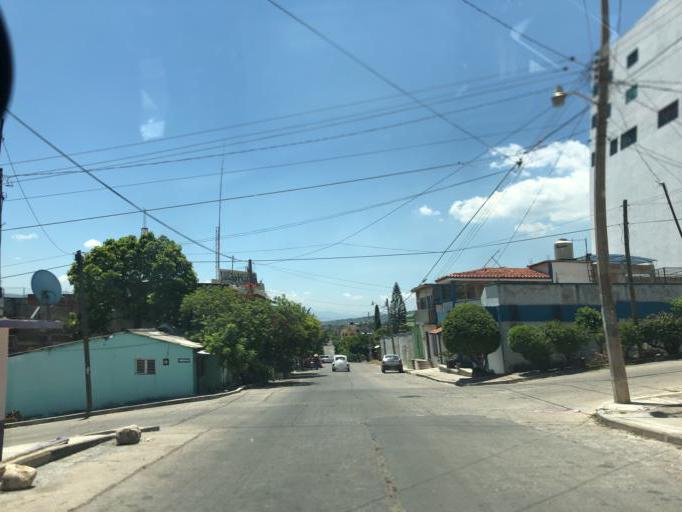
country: MX
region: Chiapas
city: Tuxtla Gutierrez
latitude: 16.7445
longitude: -93.1270
